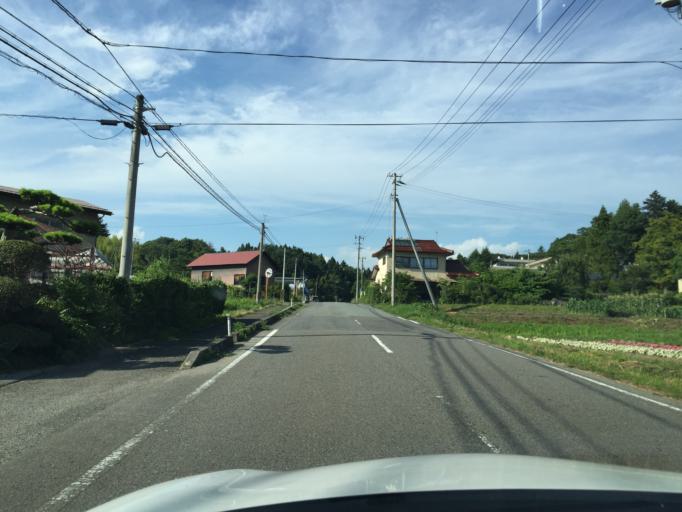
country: JP
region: Fukushima
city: Sukagawa
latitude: 37.3215
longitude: 140.4872
